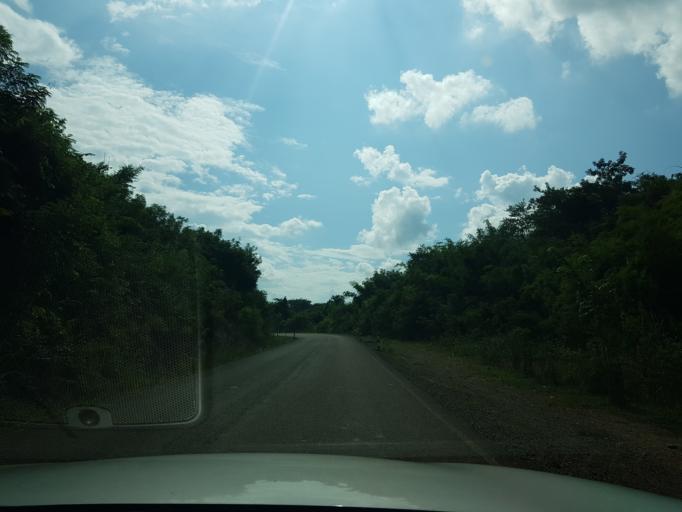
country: TH
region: Nong Khai
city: Sangkhom
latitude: 18.1887
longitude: 102.1972
